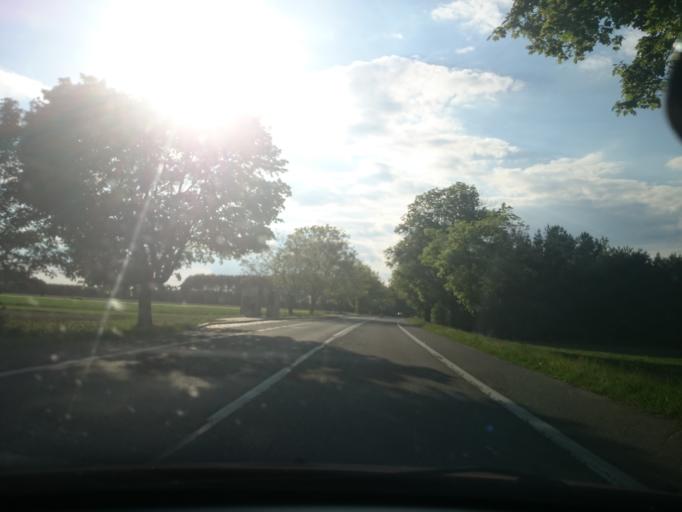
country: PL
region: Opole Voivodeship
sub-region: Powiat strzelecki
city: Izbicko
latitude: 50.5628
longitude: 18.1763
